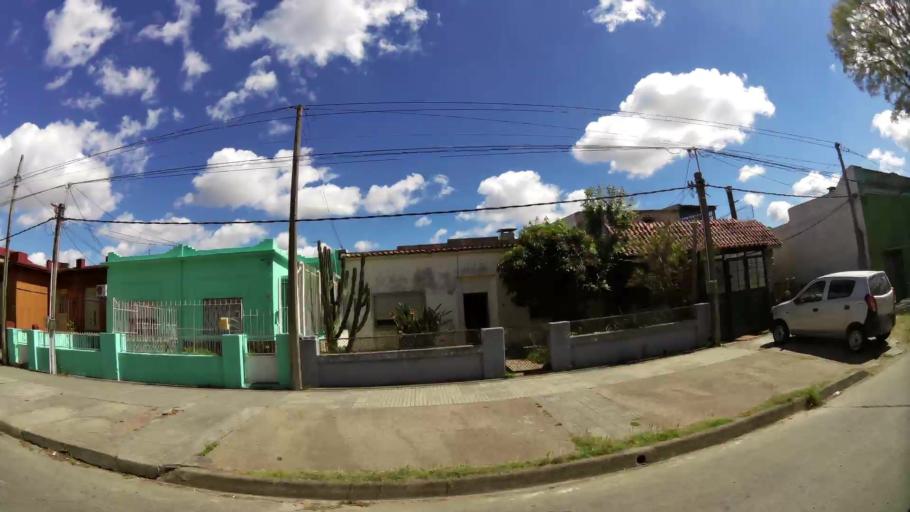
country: UY
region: Montevideo
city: Montevideo
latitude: -34.8467
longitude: -56.1329
